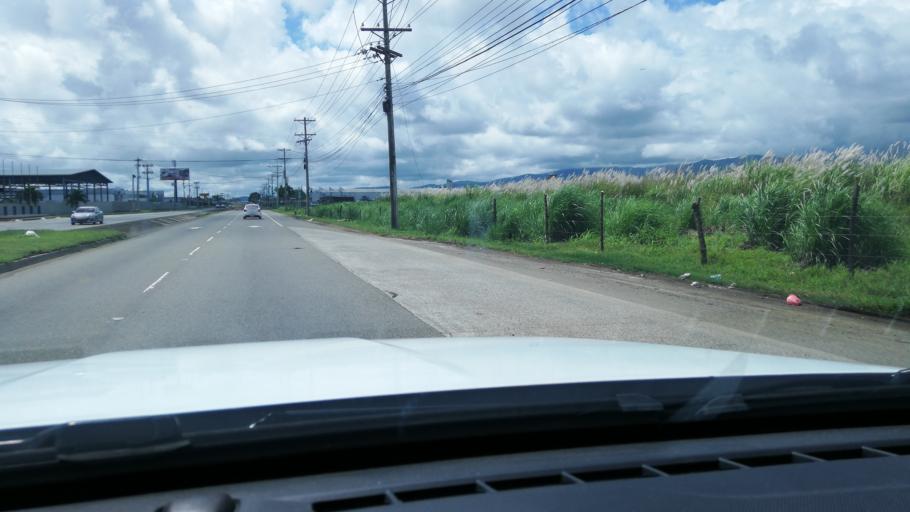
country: PA
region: Panama
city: Pacora
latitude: 9.0990
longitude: -79.3092
